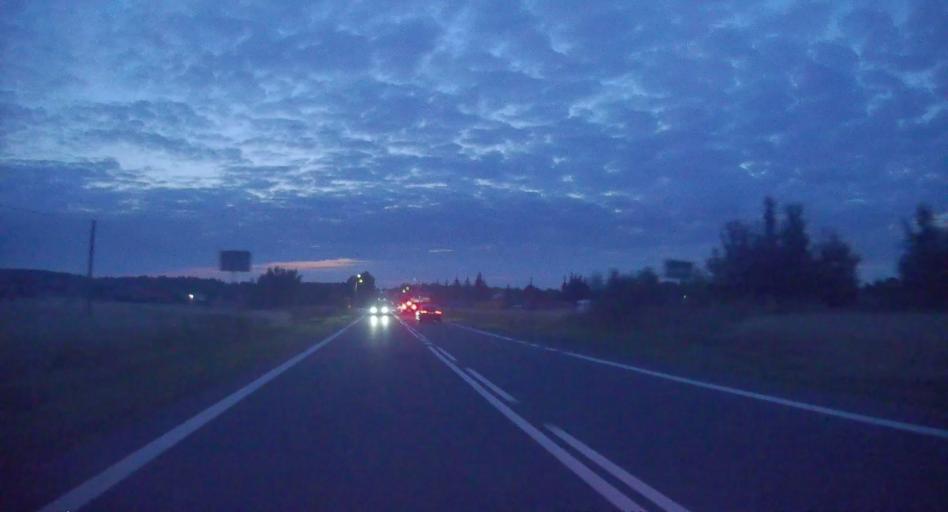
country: PL
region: Silesian Voivodeship
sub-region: Powiat klobucki
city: Kamyk
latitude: 50.8566
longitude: 19.0303
